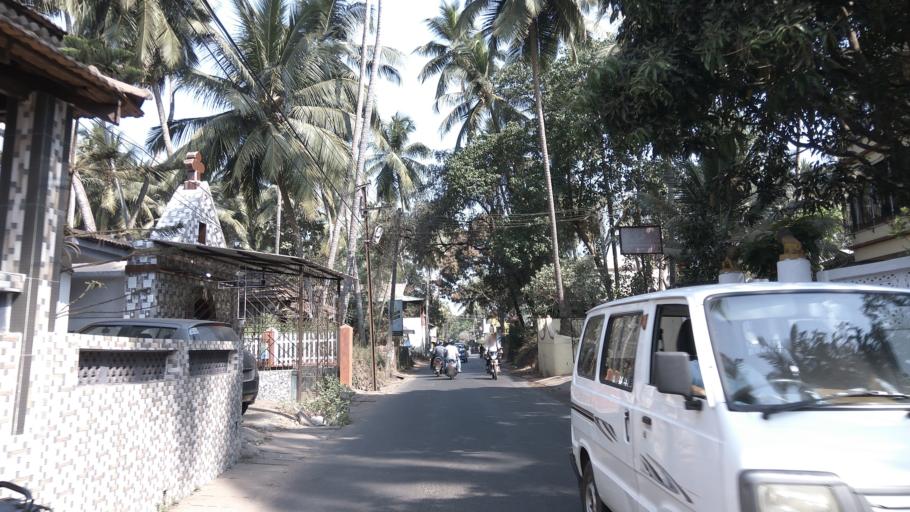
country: IN
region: Goa
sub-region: North Goa
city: Saligao
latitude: 15.5478
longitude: 73.7891
